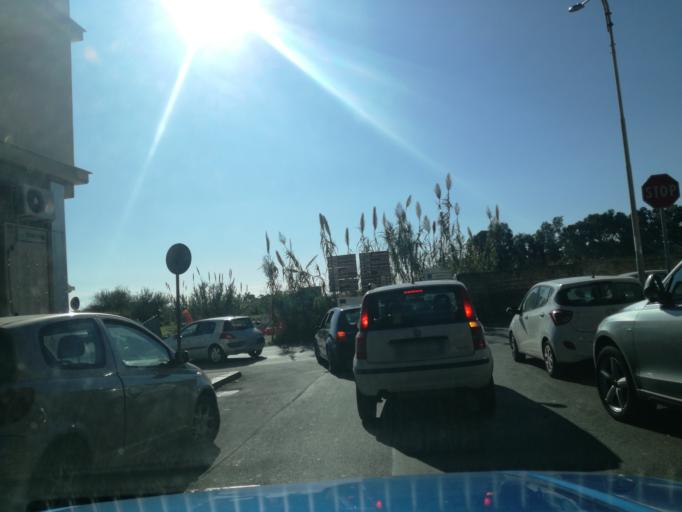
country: IT
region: Sicily
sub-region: Provincia di Caltanissetta
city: Gela
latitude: 37.0730
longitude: 14.2273
